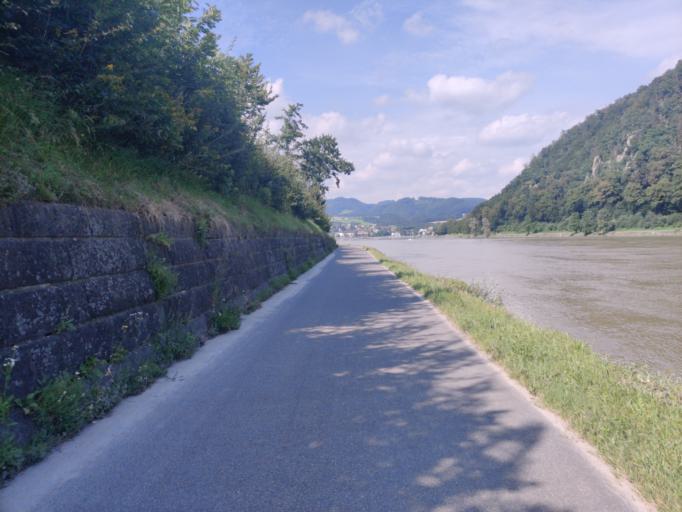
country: AT
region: Upper Austria
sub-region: Politischer Bezirk Perg
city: Bad Kreuzen
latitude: 48.2138
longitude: 14.8559
